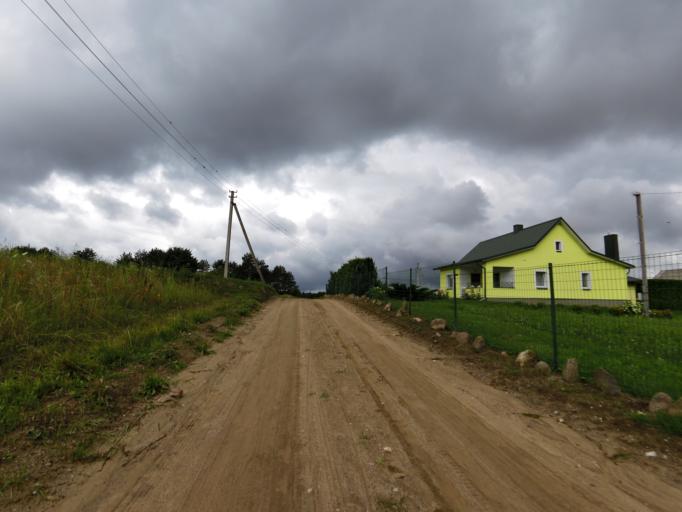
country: LT
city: Grigiskes
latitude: 54.7036
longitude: 25.1069
